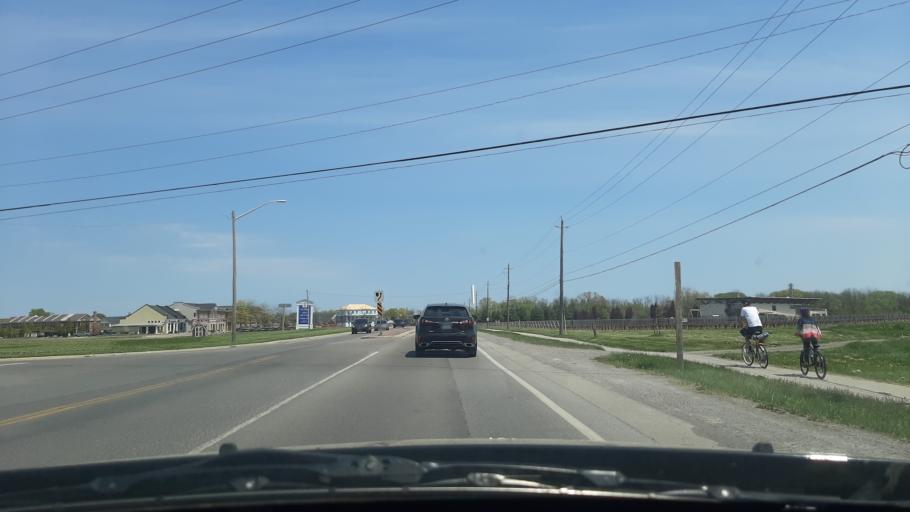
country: US
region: New York
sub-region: Niagara County
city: Youngstown
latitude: 43.2425
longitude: -79.0961
